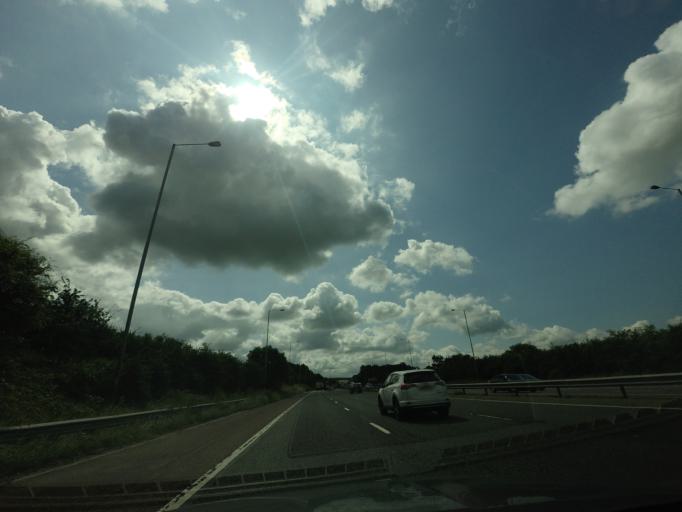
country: GB
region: England
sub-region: Lancashire
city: Euxton
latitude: 53.6535
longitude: -2.6909
